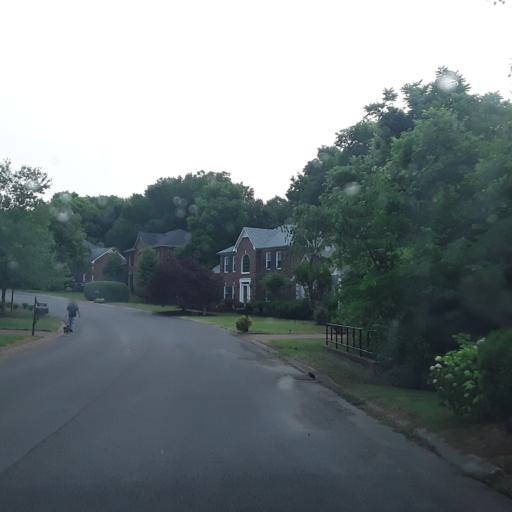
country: US
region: Tennessee
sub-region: Williamson County
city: Brentwood
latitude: 36.0459
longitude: -86.7727
